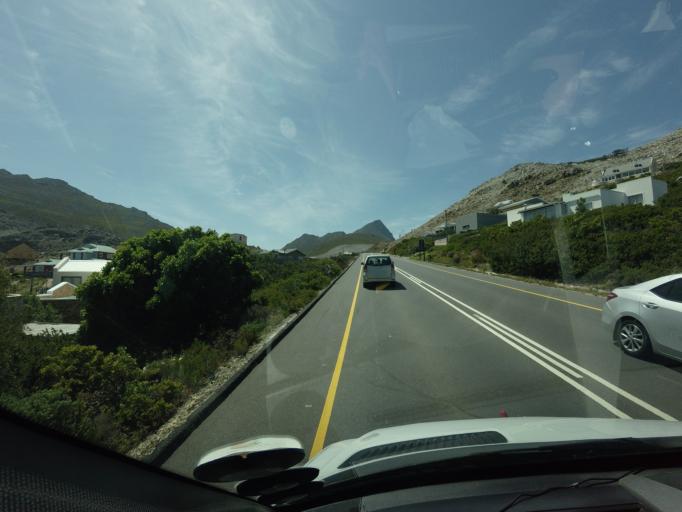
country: ZA
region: Western Cape
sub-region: Overberg District Municipality
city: Grabouw
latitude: -34.3032
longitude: 18.8223
